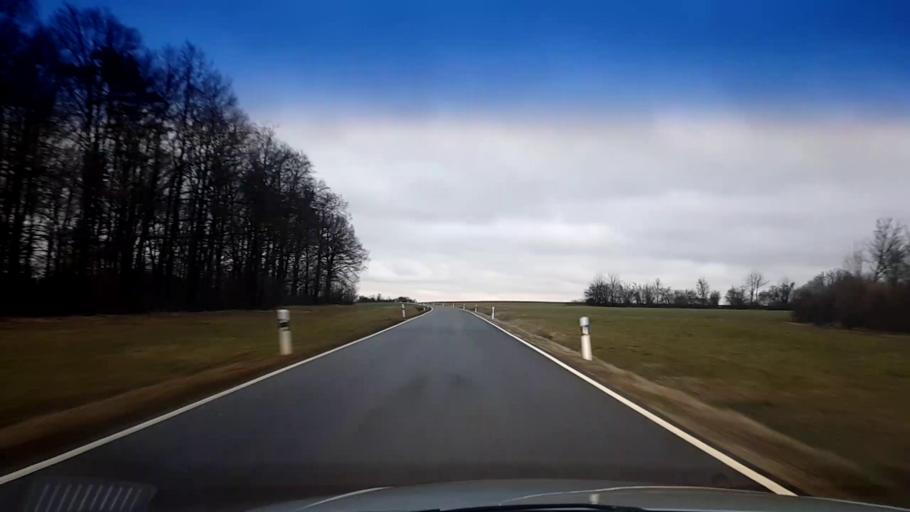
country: DE
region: Bavaria
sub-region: Upper Franconia
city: Wattendorf
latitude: 50.0354
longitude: 11.0638
